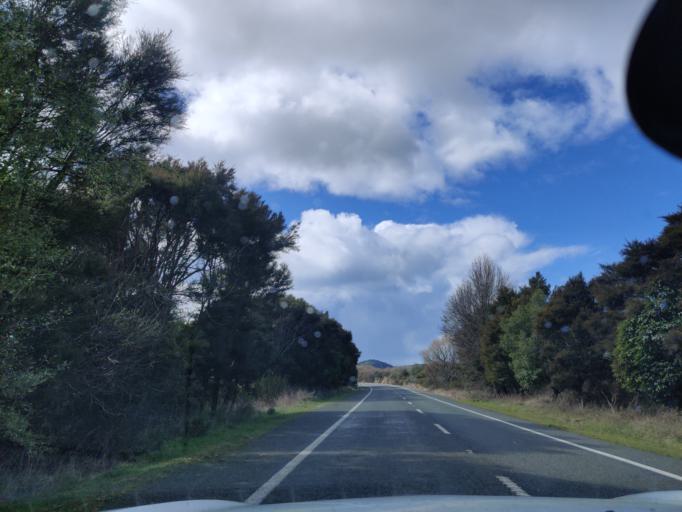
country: NZ
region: Waikato
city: Turangi
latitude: -38.9750
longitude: 175.8309
